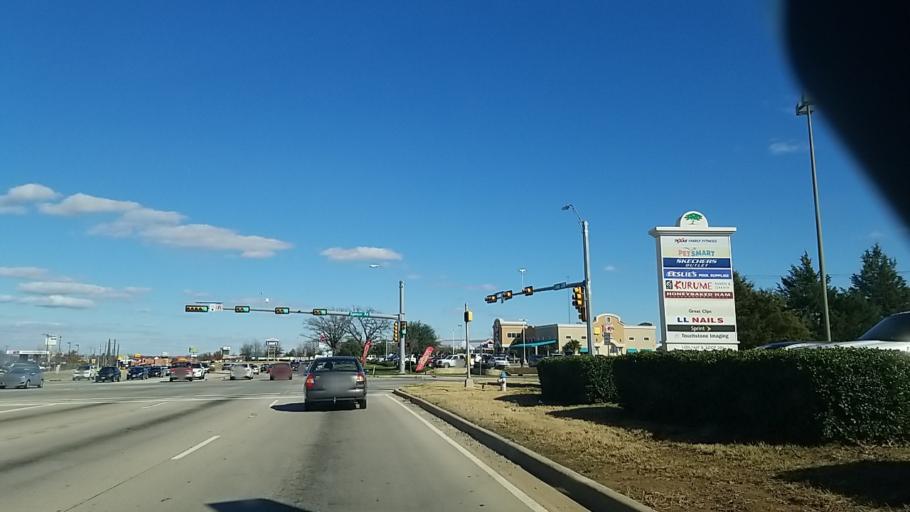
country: US
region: Texas
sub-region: Denton County
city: Denton
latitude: 33.1950
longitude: -97.0930
